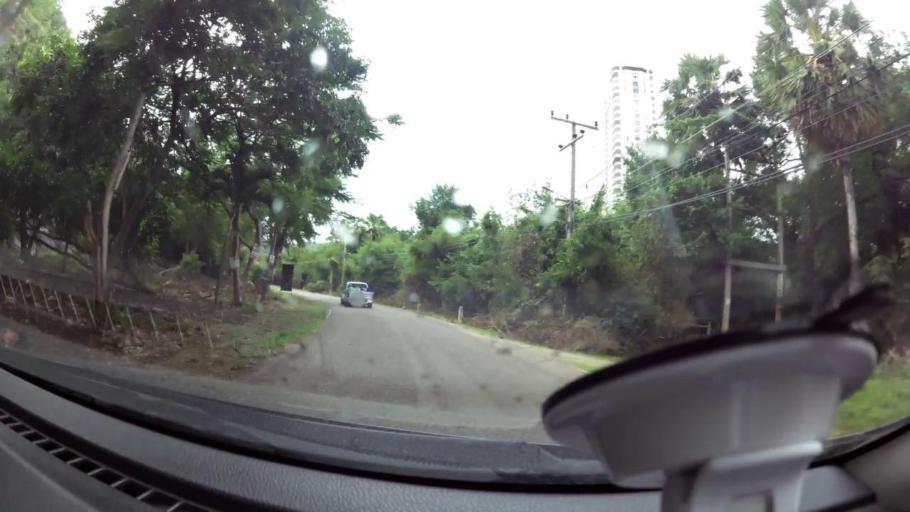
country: TH
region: Prachuap Khiri Khan
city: Pran Buri
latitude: 12.4315
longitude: 99.9789
